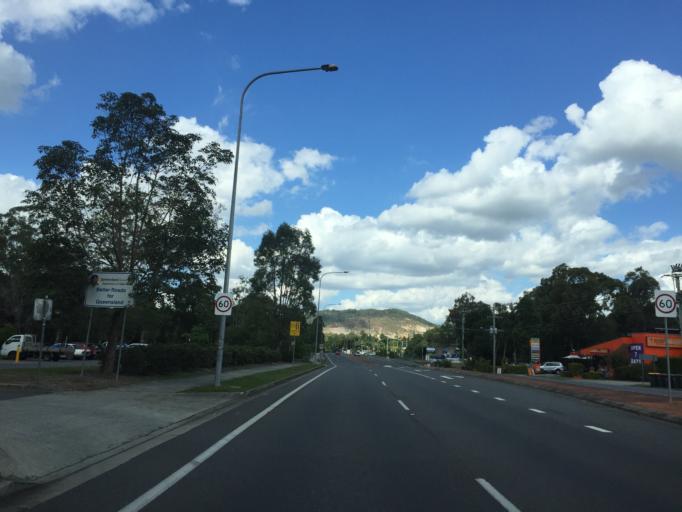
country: AU
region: Queensland
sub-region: Moreton Bay
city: Ferny Hills
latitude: -27.4021
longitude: 152.9375
